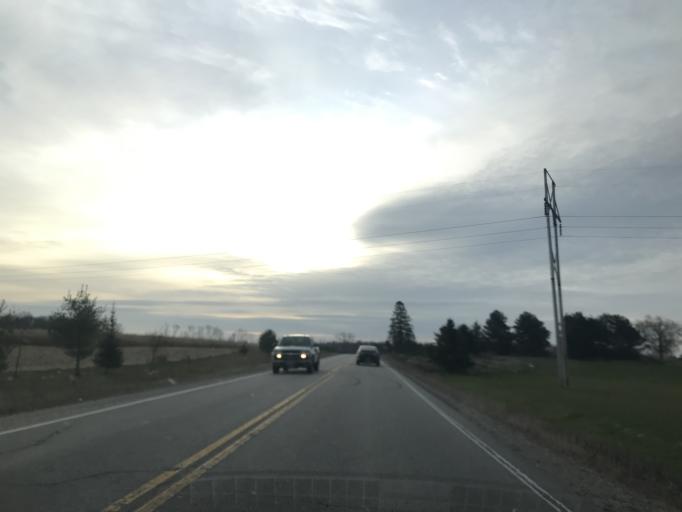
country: US
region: Wisconsin
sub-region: Marinette County
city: Peshtigo
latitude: 45.0610
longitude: -87.7983
